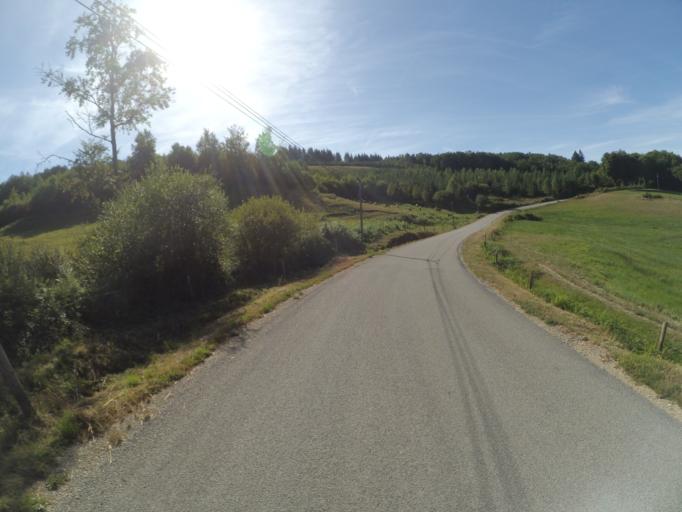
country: FR
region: Limousin
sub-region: Departement de la Correze
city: Bugeat
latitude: 45.6939
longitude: 1.8821
